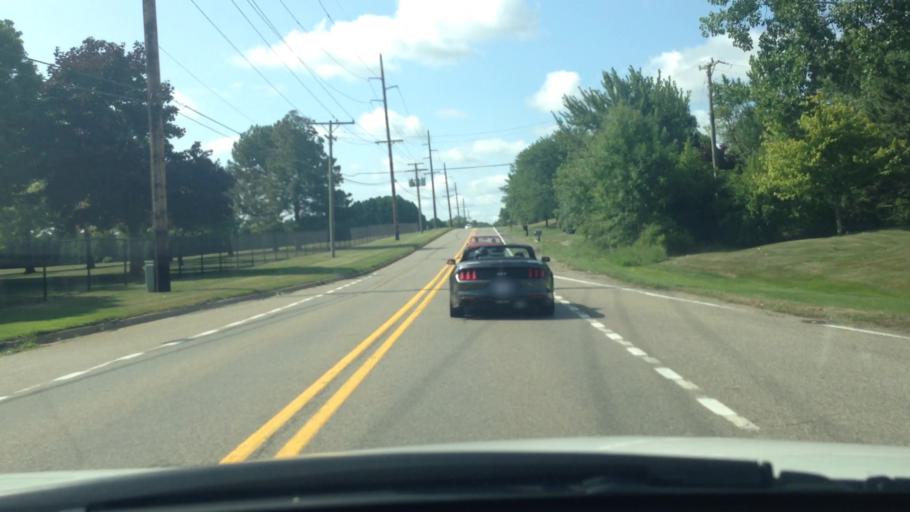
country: US
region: Michigan
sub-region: Oakland County
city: Waterford
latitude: 42.7012
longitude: -83.4417
